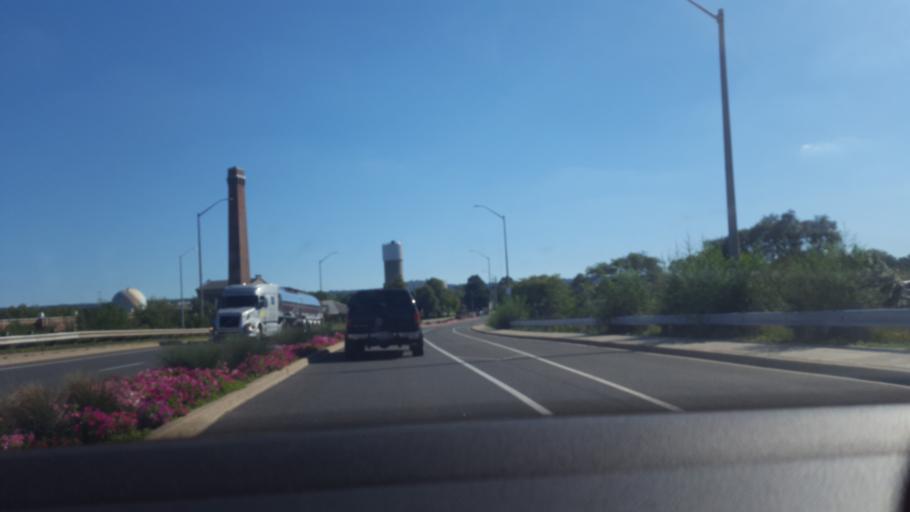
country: CA
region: Ontario
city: Hamilton
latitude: 43.2584
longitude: -79.7728
